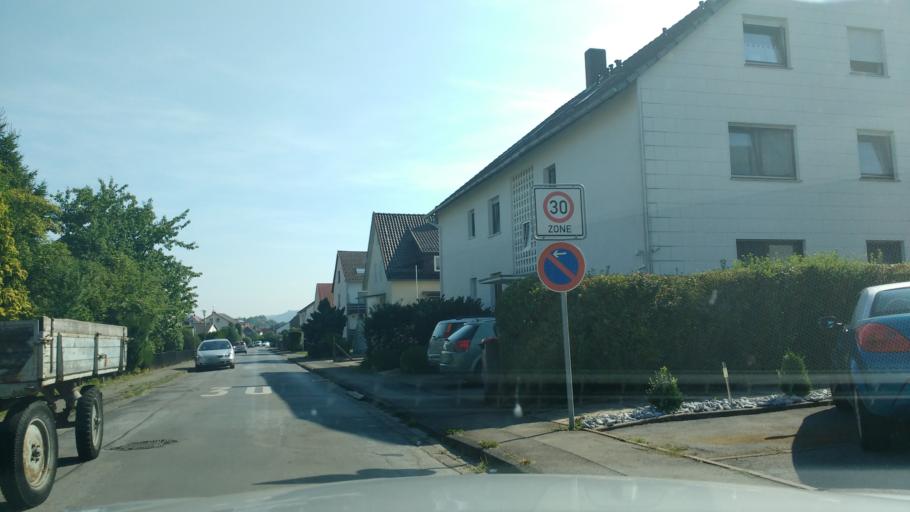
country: DE
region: Lower Saxony
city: Bad Pyrmont
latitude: 51.9806
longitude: 9.2311
